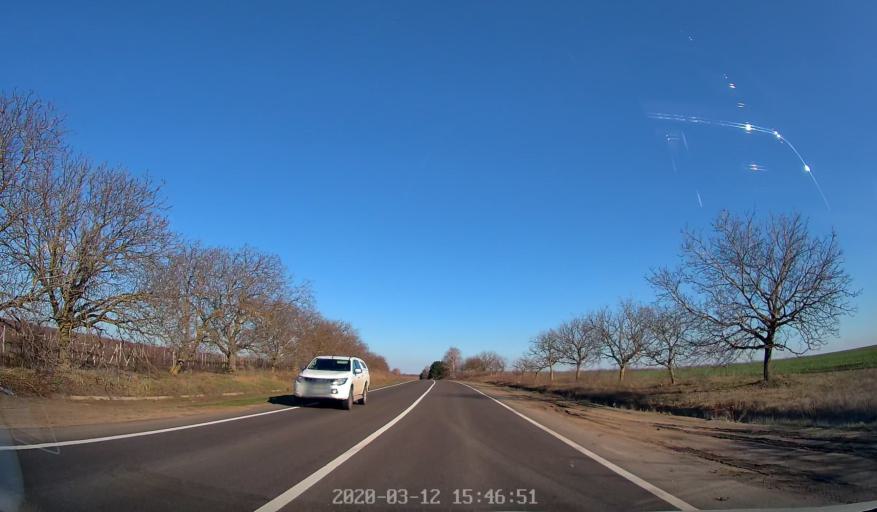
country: MD
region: Chisinau
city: Stauceni
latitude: 47.0977
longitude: 28.9001
